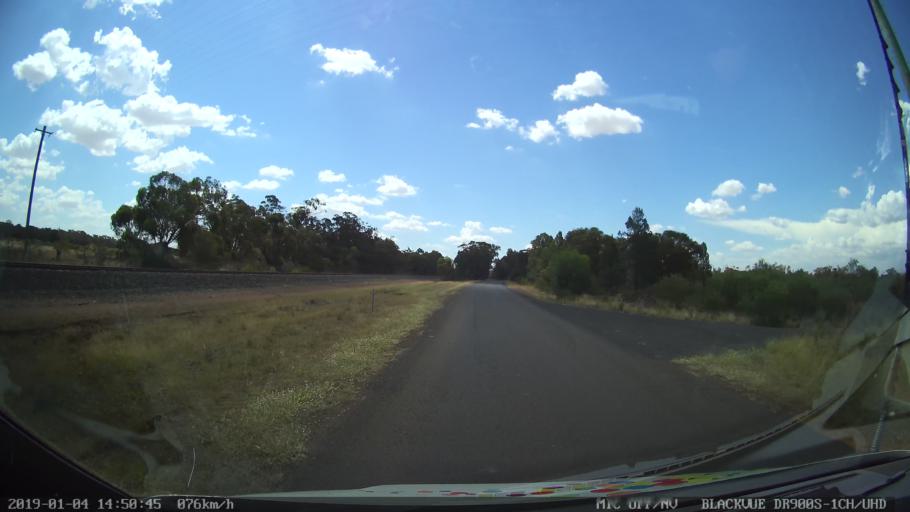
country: AU
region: New South Wales
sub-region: Dubbo Municipality
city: Dubbo
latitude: -32.0344
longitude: 148.6556
